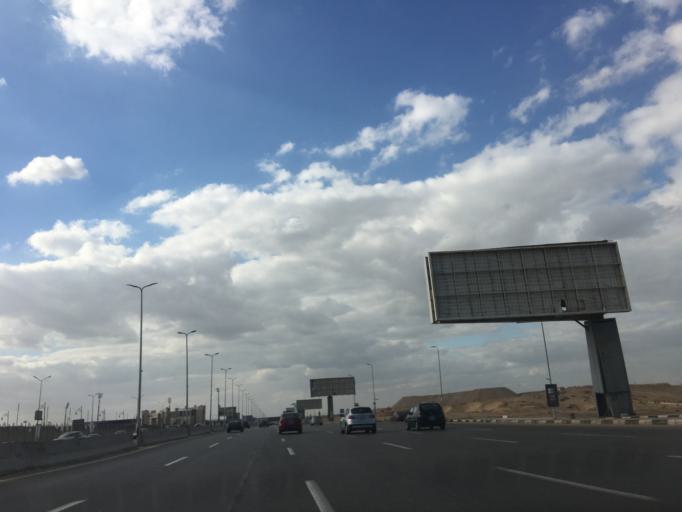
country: EG
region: Muhafazat al Qahirah
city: Cairo
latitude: 30.0196
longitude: 31.3832
